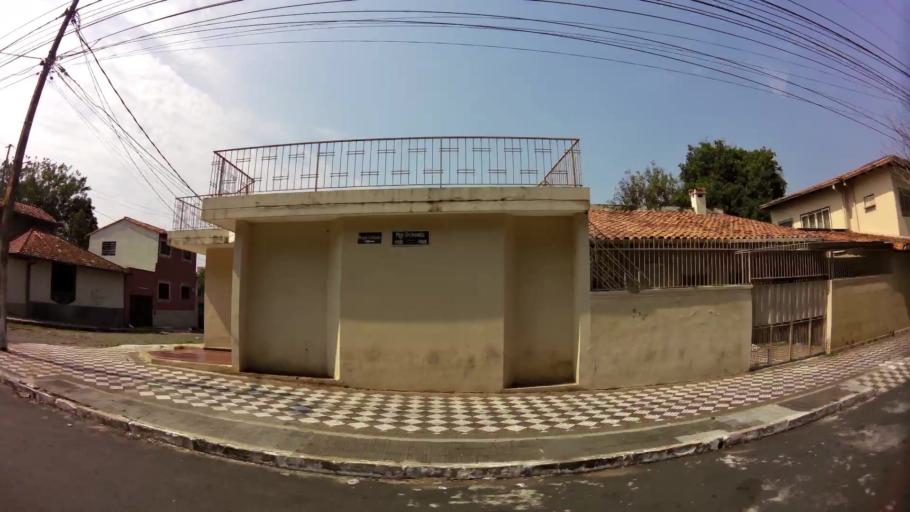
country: PY
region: Asuncion
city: Asuncion
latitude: -25.2930
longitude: -57.6574
